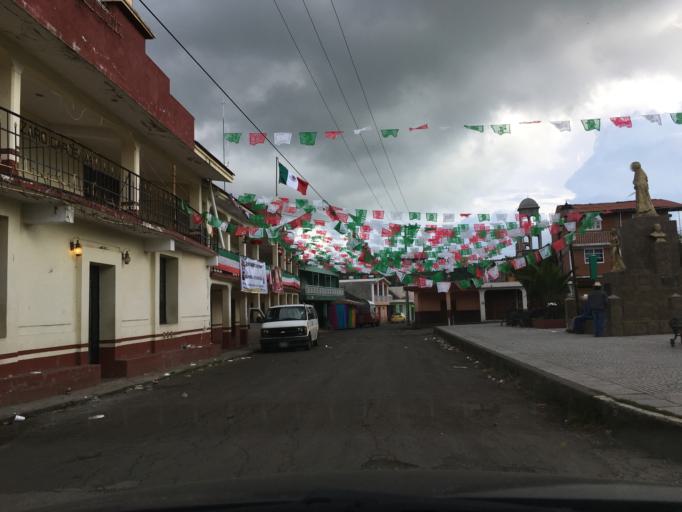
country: MX
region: Michoacan
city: Capula
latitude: 19.6440
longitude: -101.8287
